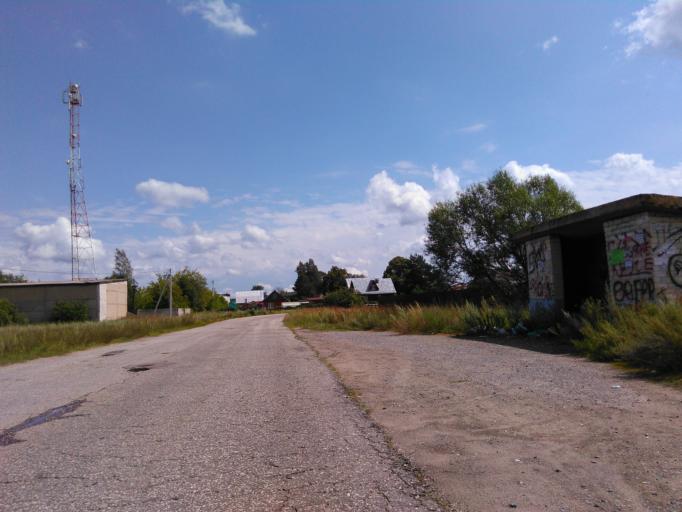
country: RU
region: Vladimir
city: Krasnyy Oktyabr'
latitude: 56.0227
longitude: 38.7971
